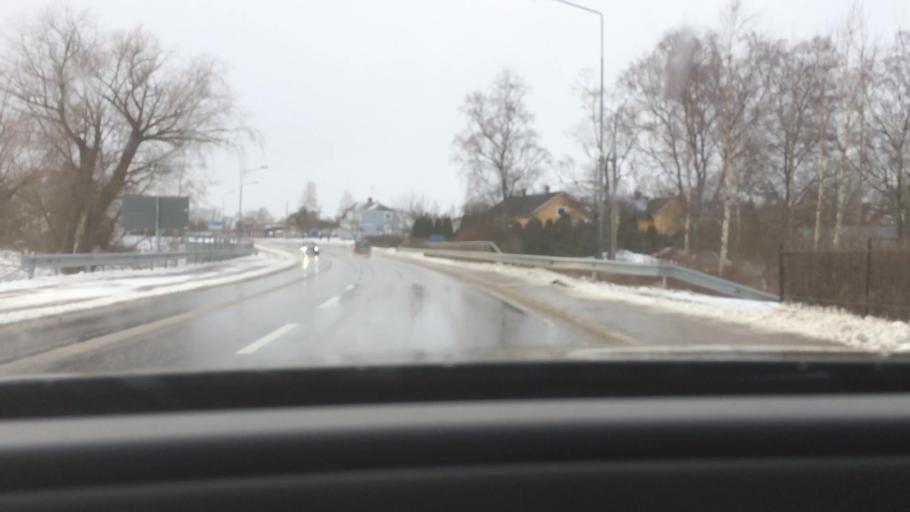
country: SE
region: Vaestra Goetaland
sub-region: Falkopings Kommun
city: Falkoeping
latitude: 57.9850
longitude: 13.5331
